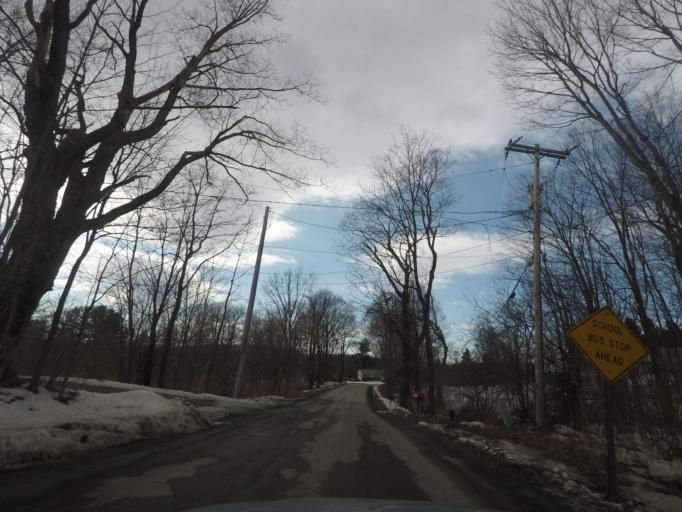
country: US
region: New York
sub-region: Saratoga County
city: Waterford
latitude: 42.7716
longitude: -73.6347
